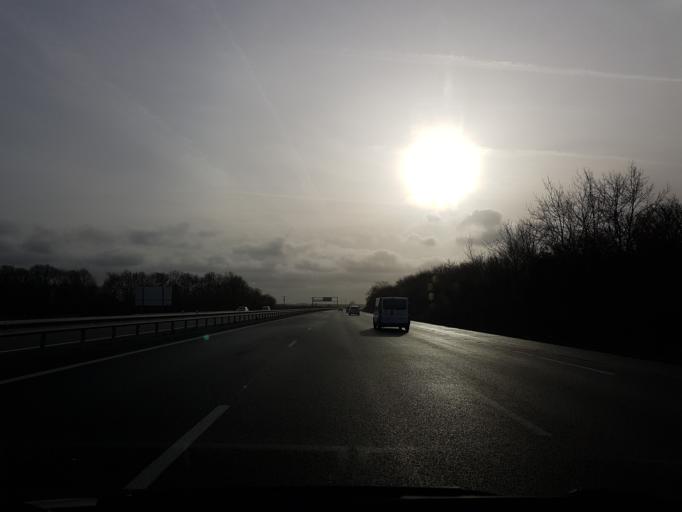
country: FR
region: Ile-de-France
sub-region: Departement de Seine-et-Marne
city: Le Chatelet-en-Brie
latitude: 48.5239
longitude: 2.8167
